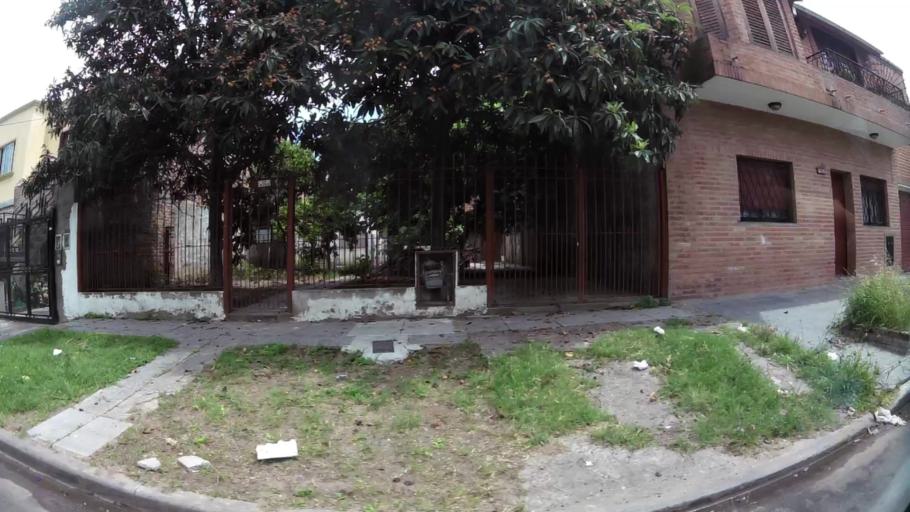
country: AR
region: Buenos Aires
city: San Justo
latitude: -34.6813
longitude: -58.5332
